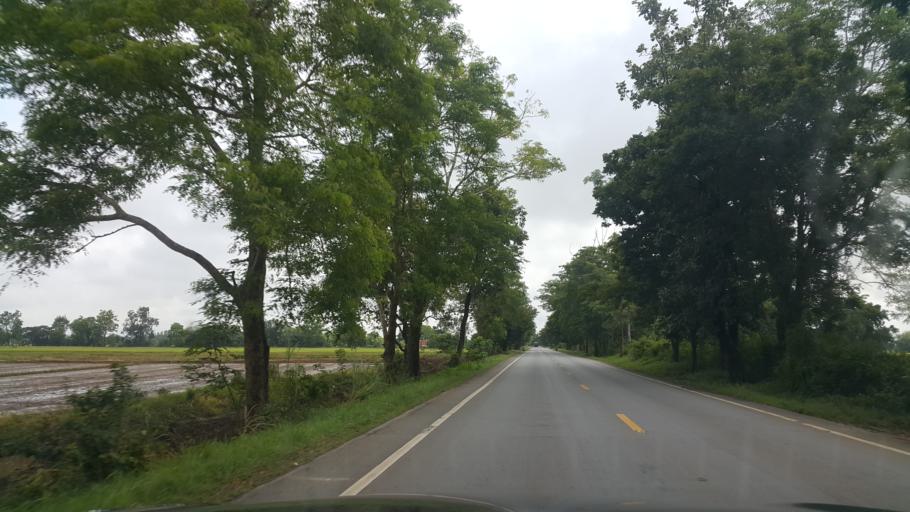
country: TH
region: Sukhothai
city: Sawankhalok
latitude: 17.3294
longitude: 99.7392
